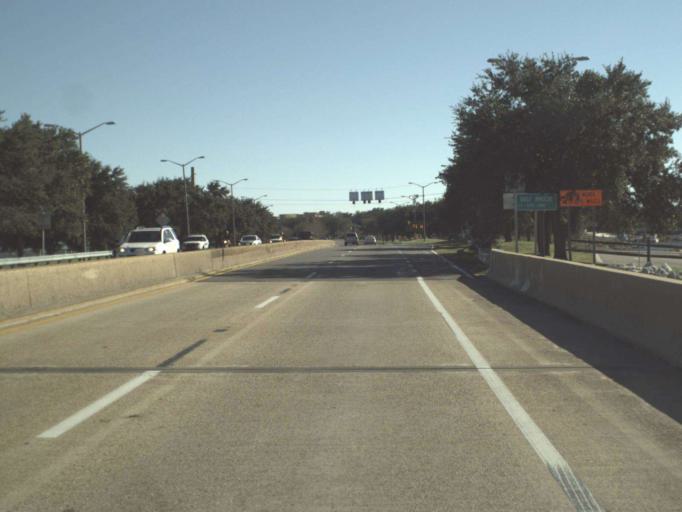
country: US
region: Florida
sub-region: Santa Rosa County
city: Gulf Breeze
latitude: 30.3740
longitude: -87.1775
